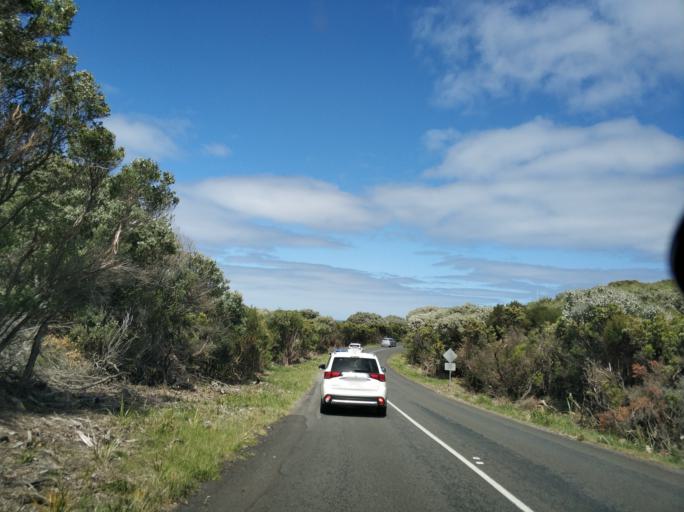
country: AU
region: Victoria
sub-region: Colac-Otway
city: Apollo Bay
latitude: -38.8535
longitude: 143.5197
